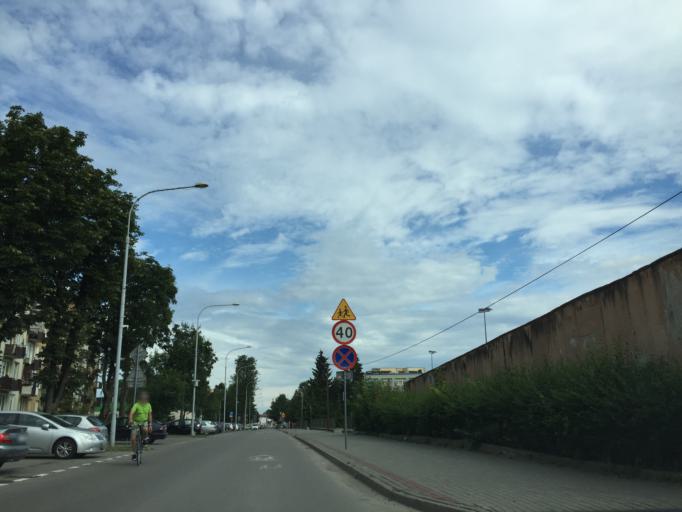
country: PL
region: Lublin Voivodeship
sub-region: Powiat lukowski
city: Lukow
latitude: 51.9341
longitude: 22.3816
